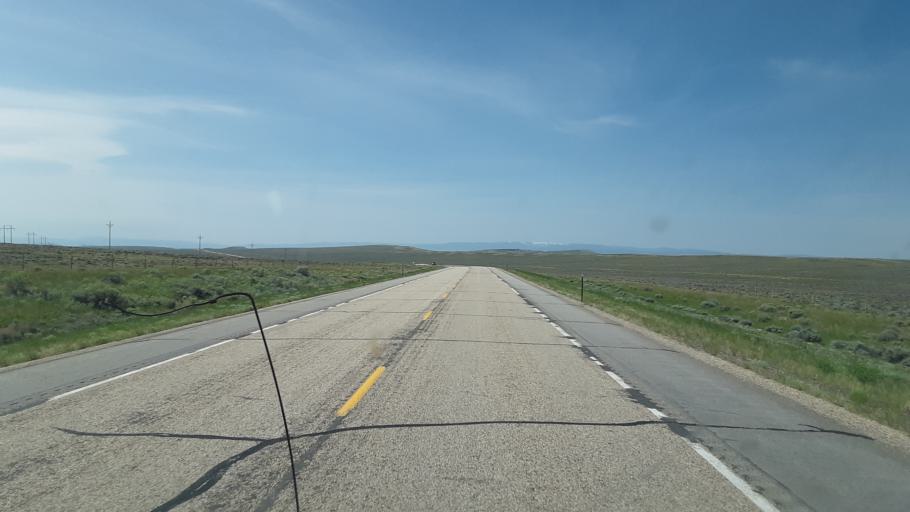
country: US
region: Wyoming
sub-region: Carbon County
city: Saratoga
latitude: 41.6127
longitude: -106.8159
